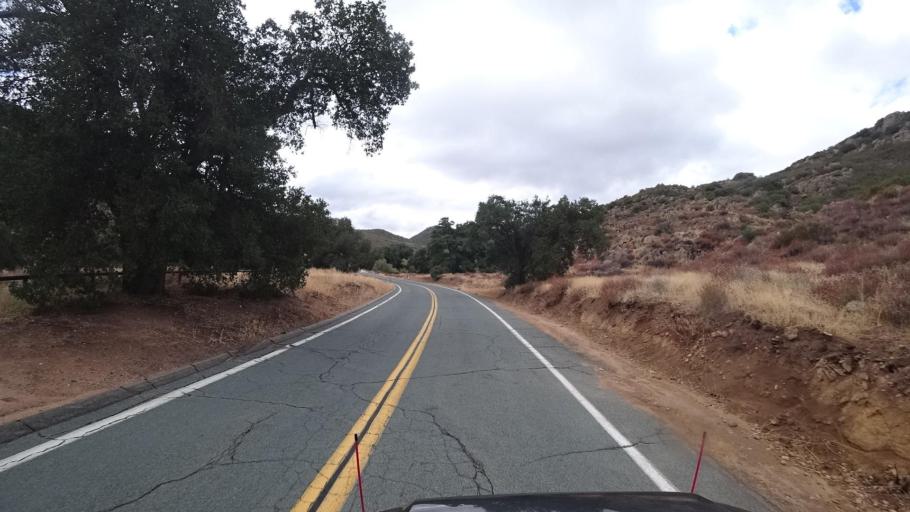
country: US
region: California
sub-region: San Diego County
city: Pine Valley
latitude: 32.7537
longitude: -116.4522
